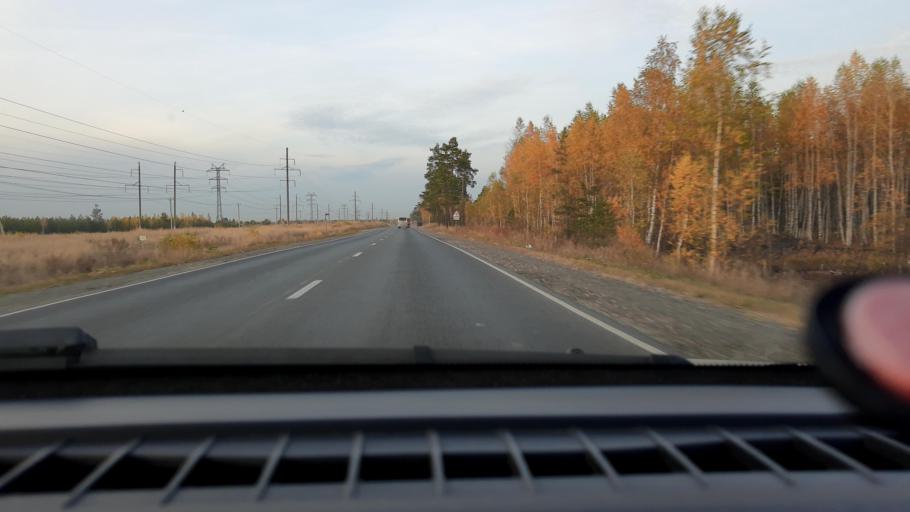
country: RU
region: Nizjnij Novgorod
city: Babino
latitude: 56.3159
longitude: 43.5591
